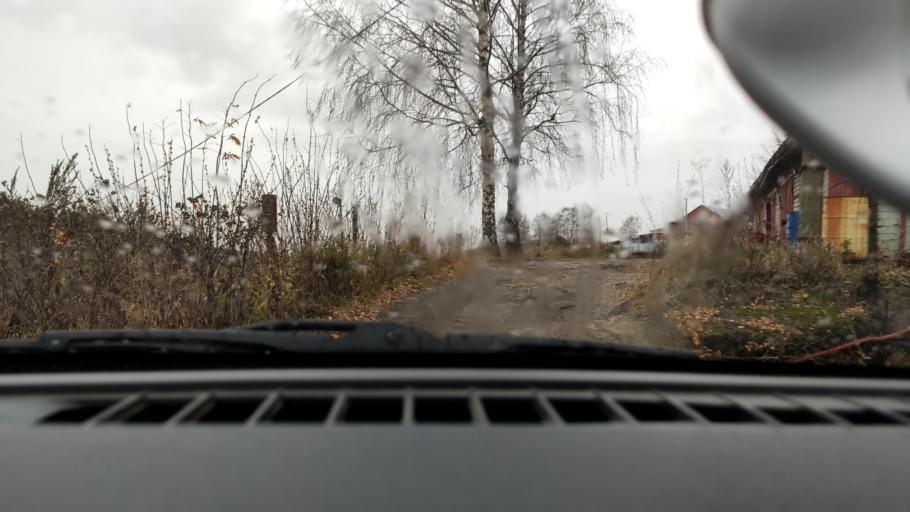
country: RU
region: Perm
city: Kondratovo
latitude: 57.9591
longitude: 56.1673
